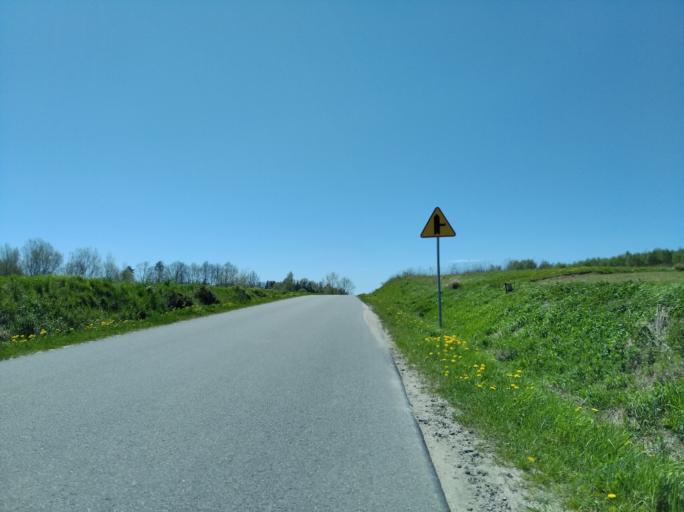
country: PL
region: Subcarpathian Voivodeship
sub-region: Powiat debicki
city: Brzostek
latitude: 49.9084
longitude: 21.4081
